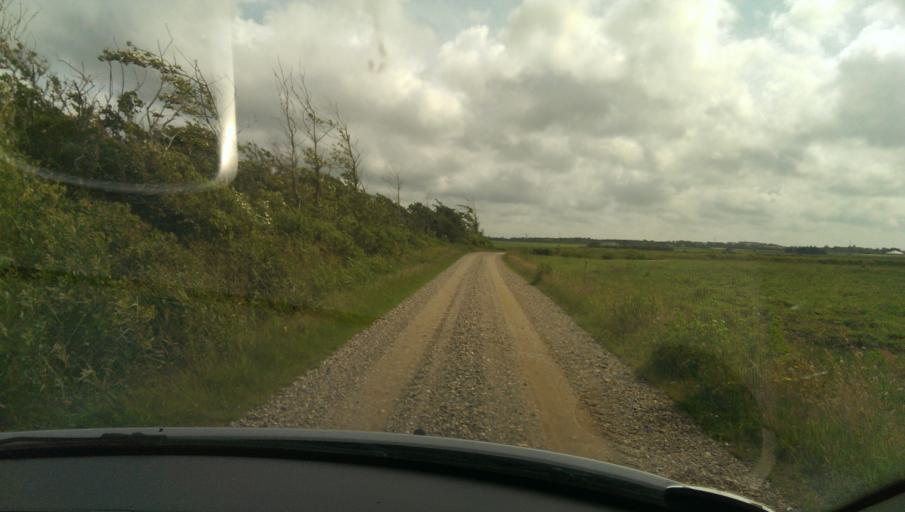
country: DK
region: Central Jutland
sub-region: Holstebro Kommune
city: Ulfborg
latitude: 56.2890
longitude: 8.2816
